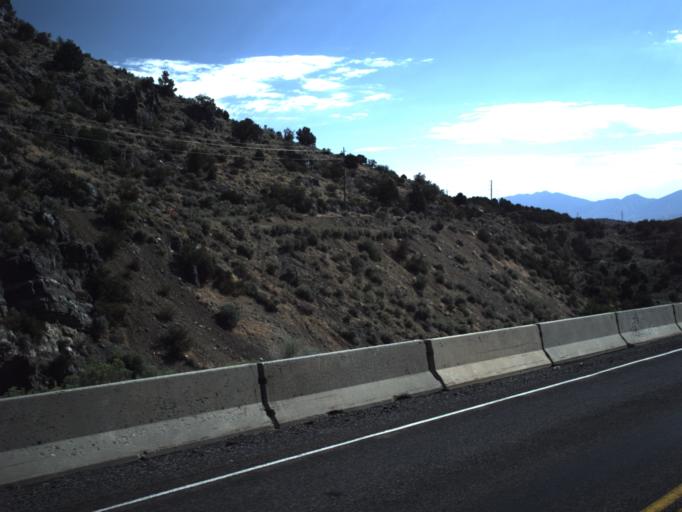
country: US
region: Utah
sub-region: Utah County
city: Genola
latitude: 39.9758
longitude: -112.0736
